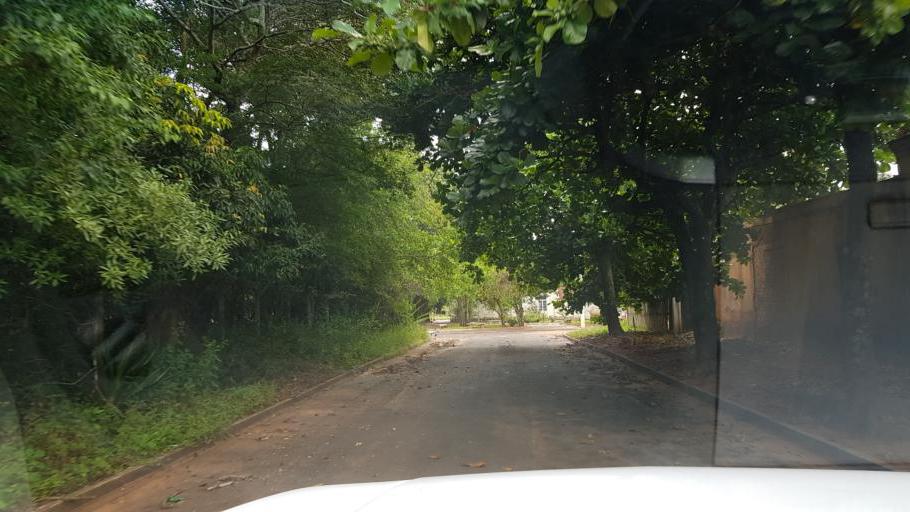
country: BR
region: Sao Paulo
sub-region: Paraguacu Paulista
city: Paraguacu Paulista
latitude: -22.3521
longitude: -50.6220
